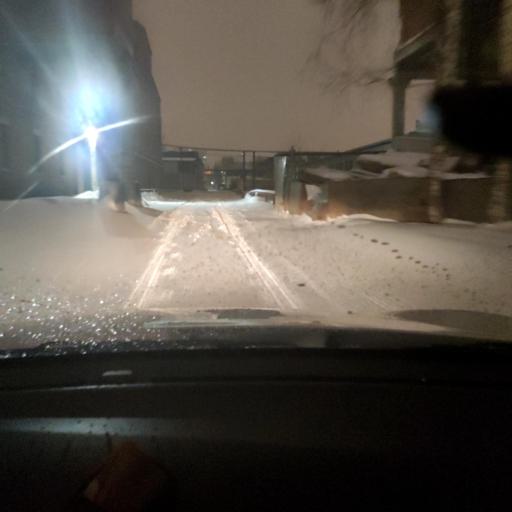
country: RU
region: Tatarstan
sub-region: Gorod Kazan'
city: Kazan
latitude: 55.8356
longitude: 49.0530
